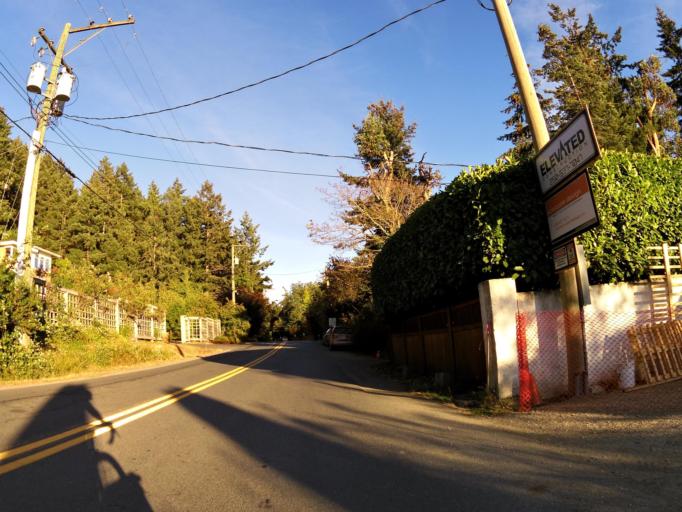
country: CA
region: British Columbia
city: North Cowichan
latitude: 48.8811
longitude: -123.5710
